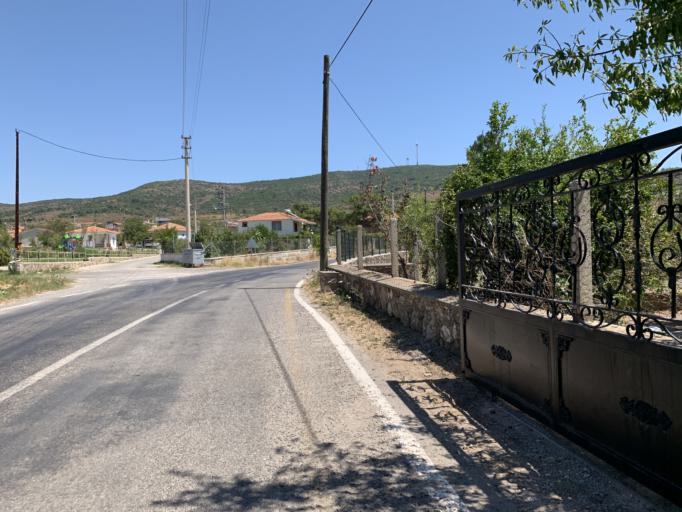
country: TR
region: Izmir
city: Uzunkuyu
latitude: 38.3222
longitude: 26.5771
